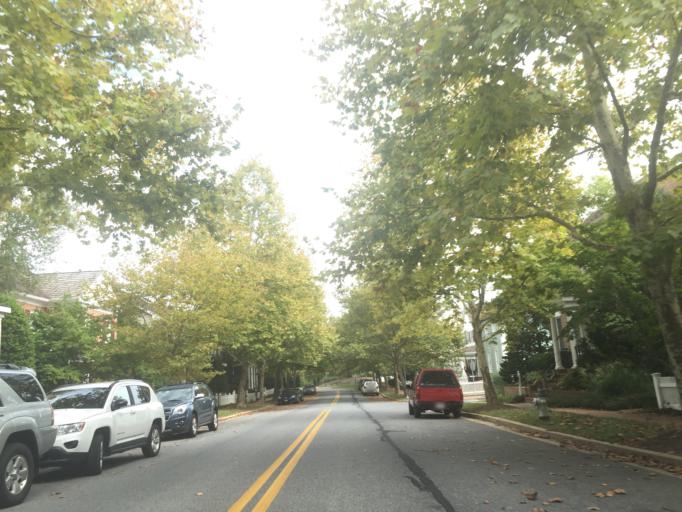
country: US
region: Maryland
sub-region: Montgomery County
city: North Potomac
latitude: 39.1163
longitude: -77.2430
